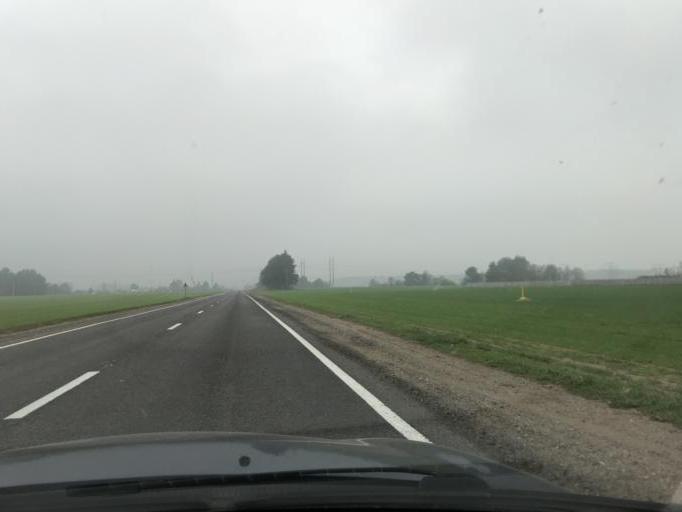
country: BY
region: Grodnenskaya
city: Hrodna
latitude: 53.8275
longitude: 23.8793
